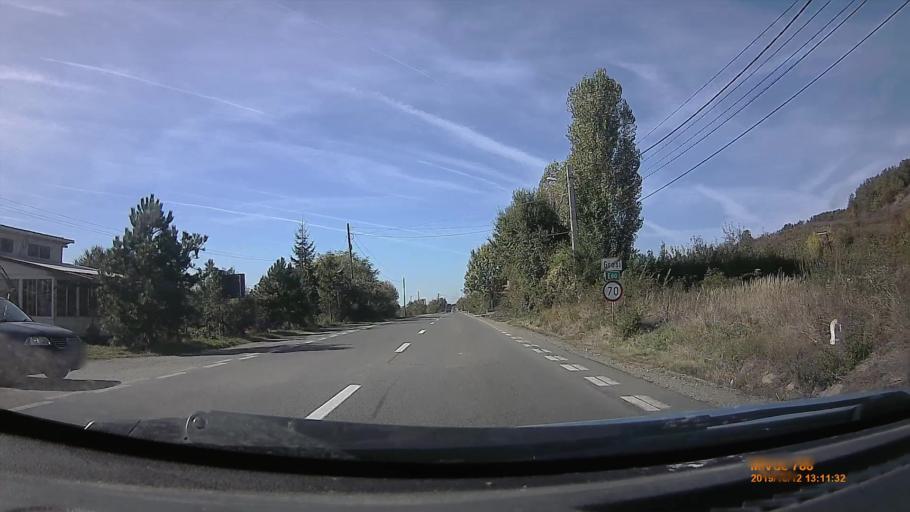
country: RO
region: Bihor
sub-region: Comuna Auseu
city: Grosi
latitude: 47.0502
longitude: 22.4550
